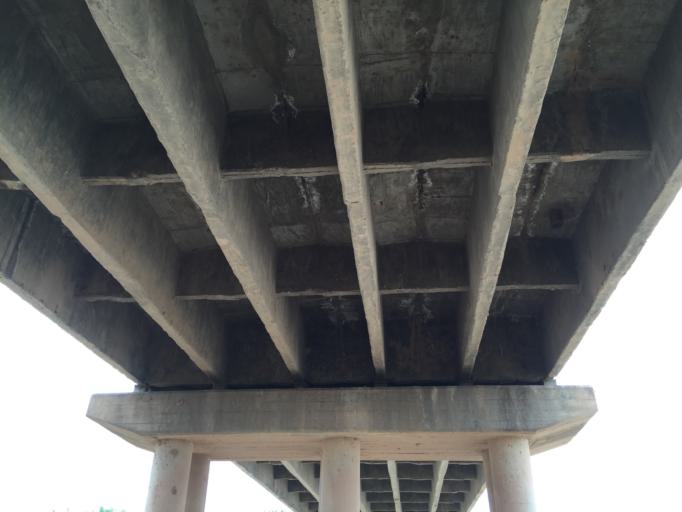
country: TJ
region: Khatlon
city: Vose'
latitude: 37.7857
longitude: 69.5680
